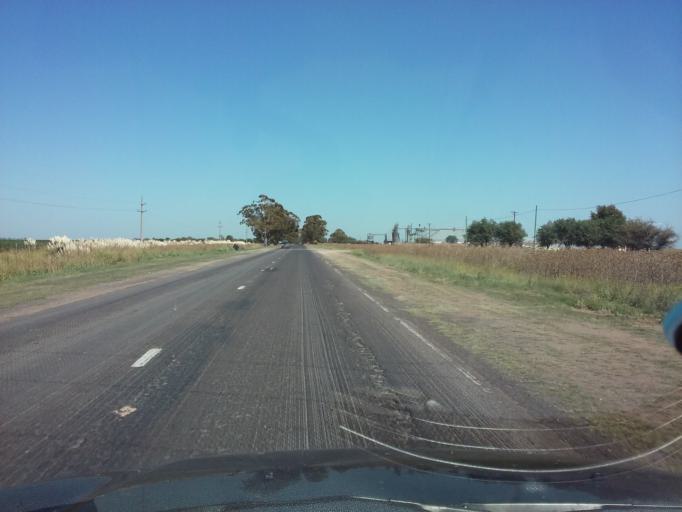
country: AR
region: La Pampa
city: General Pico
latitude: -35.6983
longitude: -63.7939
